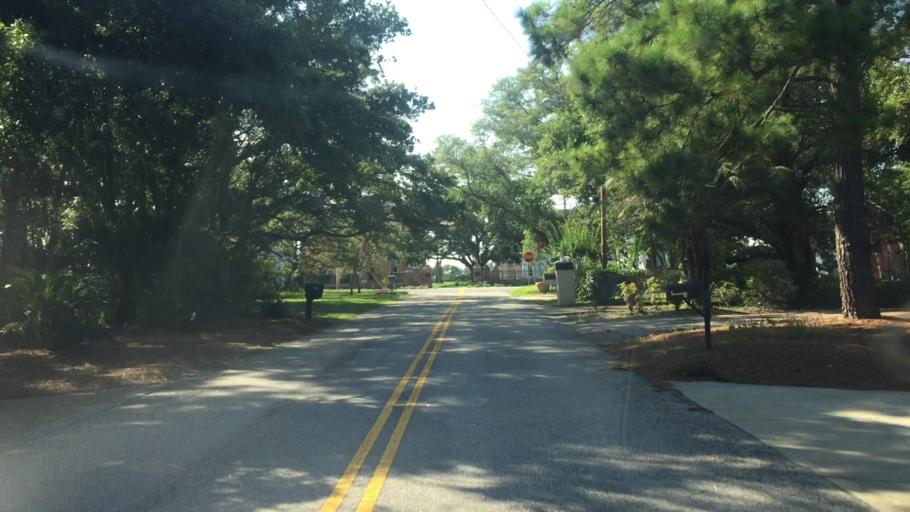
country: US
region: South Carolina
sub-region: Horry County
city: Myrtle Beach
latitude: 33.7455
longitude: -78.8137
